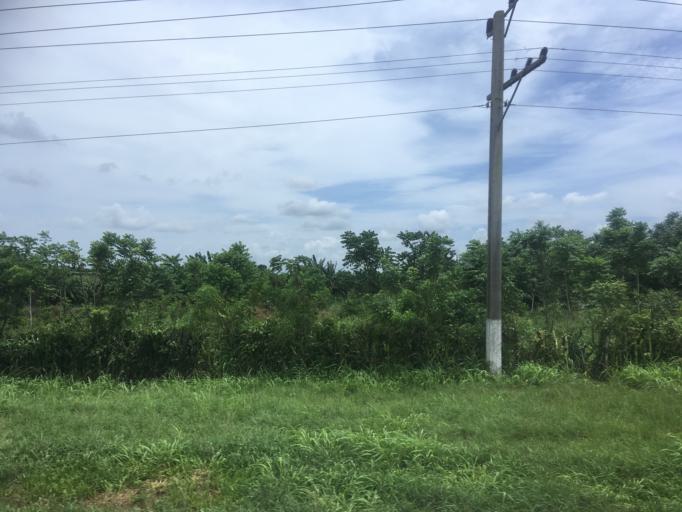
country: CU
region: Matanzas
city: Colon
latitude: 22.7037
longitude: -80.8759
